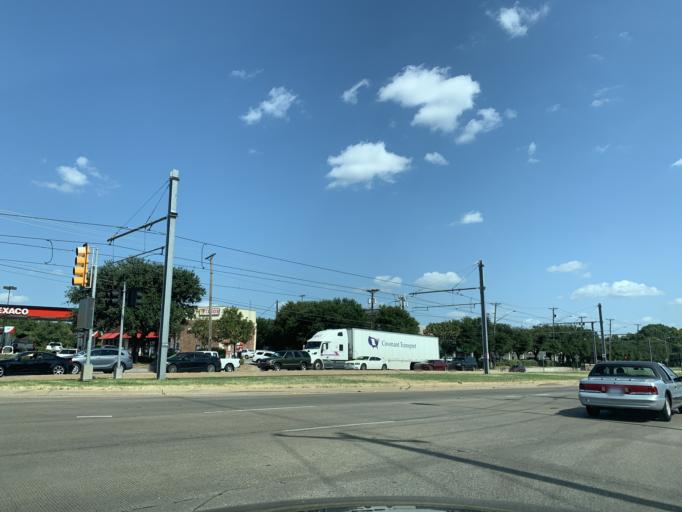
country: US
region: Texas
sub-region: Dallas County
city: Hutchins
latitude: 32.6861
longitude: -96.7900
